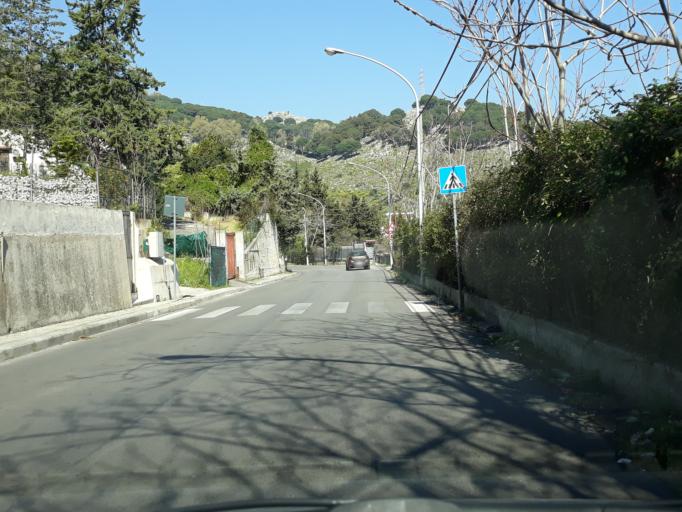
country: IT
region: Sicily
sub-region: Palermo
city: Piano dei Geli
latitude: 38.1158
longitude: 13.2901
